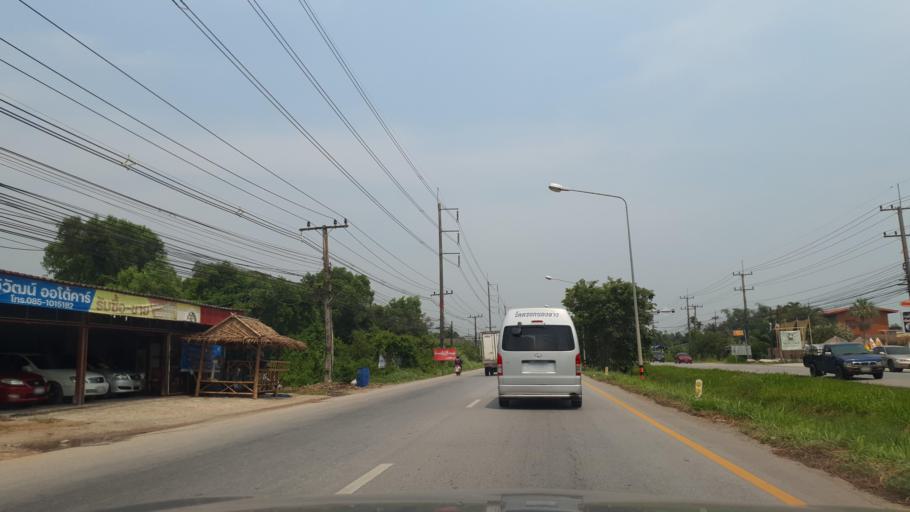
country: TH
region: Rayong
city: Rayong
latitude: 12.6431
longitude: 101.3556
